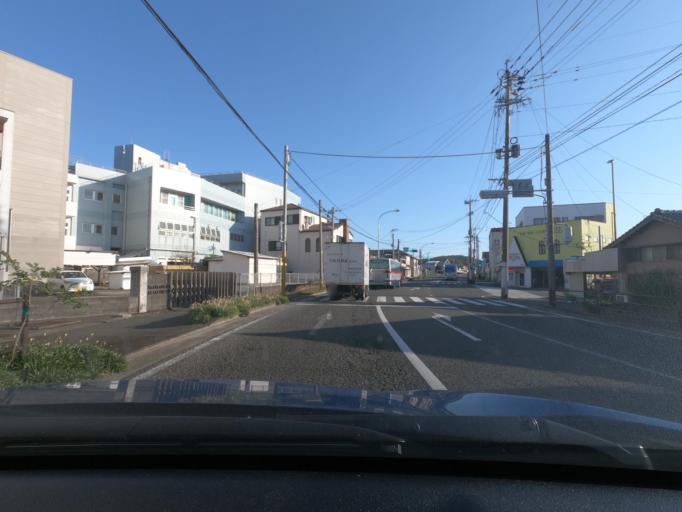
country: JP
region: Kagoshima
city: Akune
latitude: 32.0182
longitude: 130.1971
